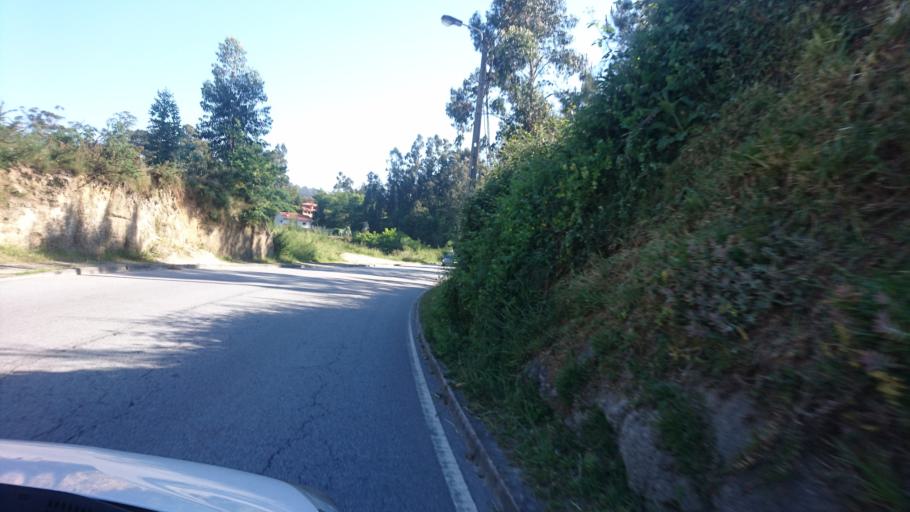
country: PT
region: Porto
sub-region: Paredes
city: Baltar
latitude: 41.1798
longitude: -8.3488
